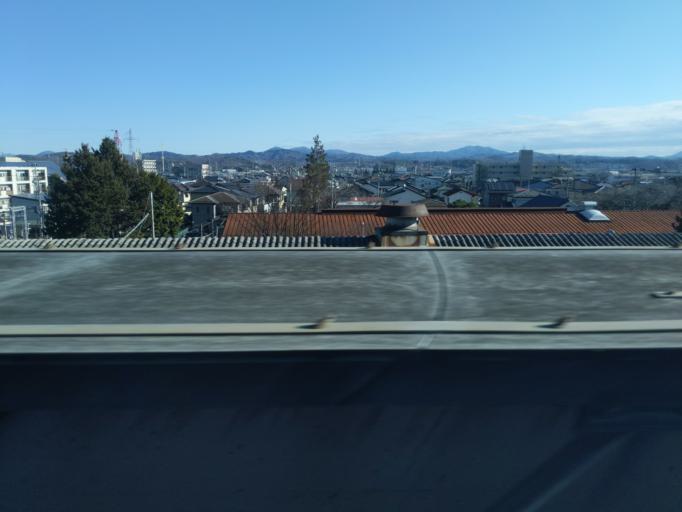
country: JP
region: Fukushima
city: Koriyama
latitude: 37.3865
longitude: 140.3857
